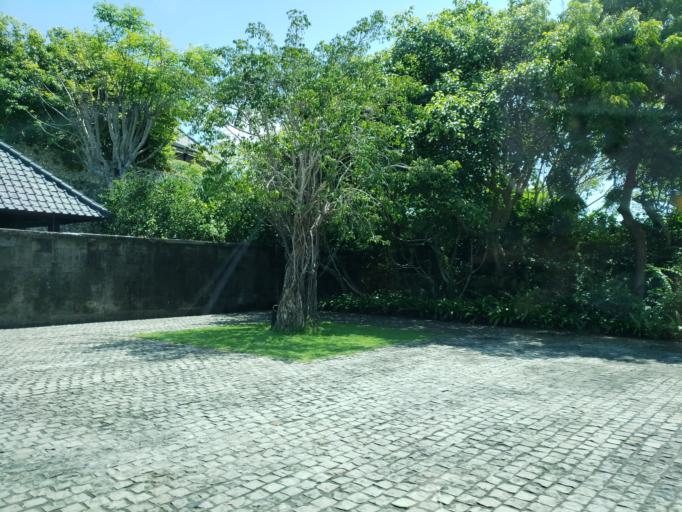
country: ID
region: Bali
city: Pecatu
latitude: -8.8431
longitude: 115.1214
